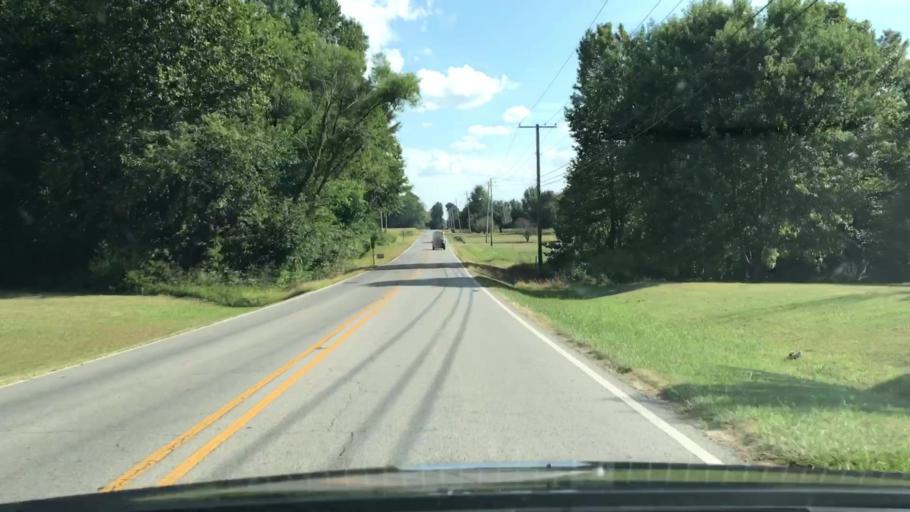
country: US
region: Alabama
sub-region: Madison County
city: Harvest
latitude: 34.8466
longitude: -86.7492
